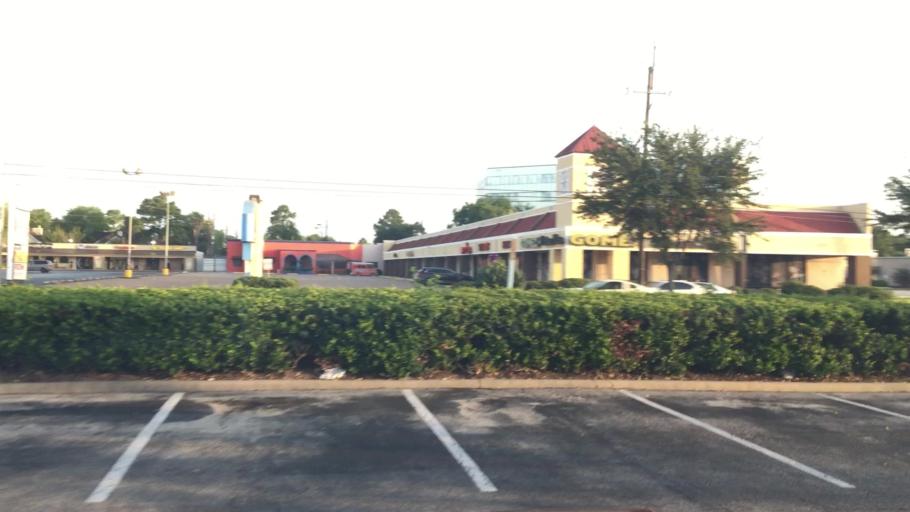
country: US
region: Texas
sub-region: Harris County
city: Hudson
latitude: 29.9863
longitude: -95.5005
